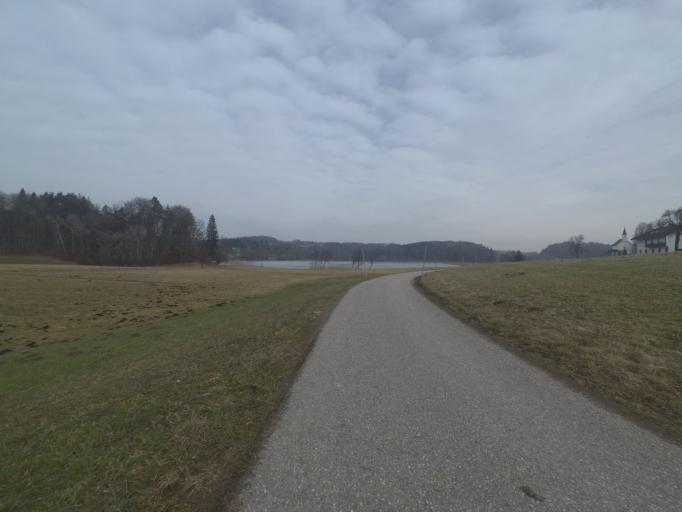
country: AT
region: Salzburg
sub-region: Politischer Bezirk Salzburg-Umgebung
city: Lamprechtshausen
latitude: 48.0691
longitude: 12.9444
